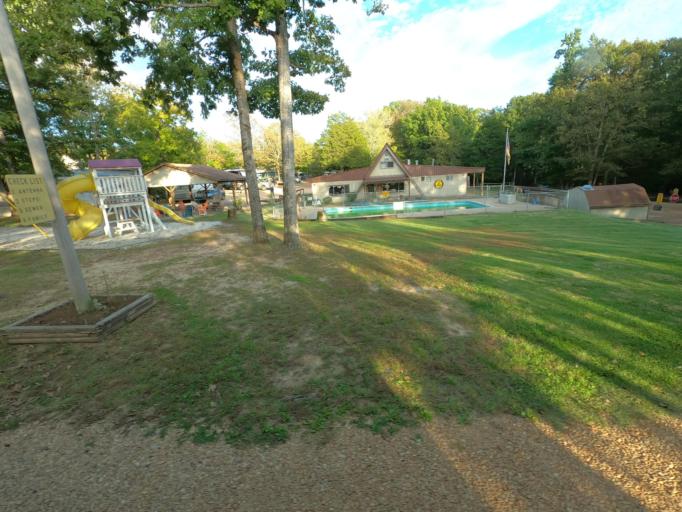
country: US
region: Tennessee
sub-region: Humphreys County
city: Waverly
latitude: 35.8808
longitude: -87.7923
